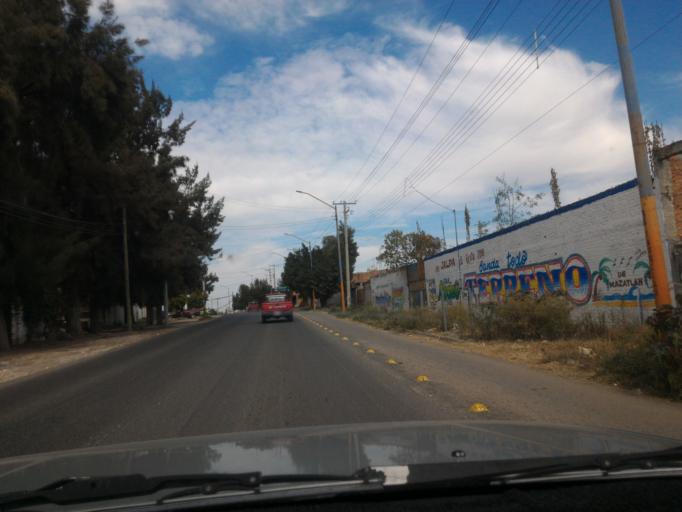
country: MX
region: Guanajuato
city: Ciudad Manuel Doblado
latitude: 20.7350
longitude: -101.9522
